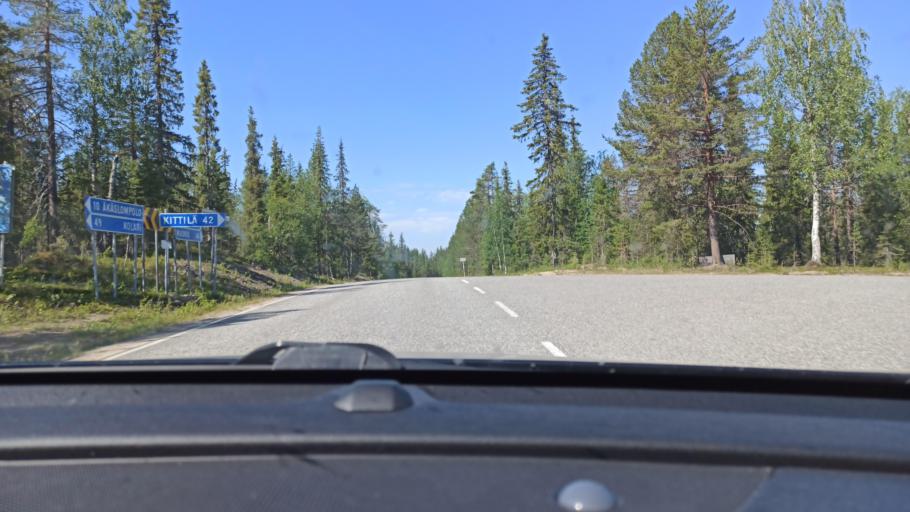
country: FI
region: Lapland
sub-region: Tunturi-Lappi
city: Kolari
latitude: 67.6841
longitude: 24.1112
